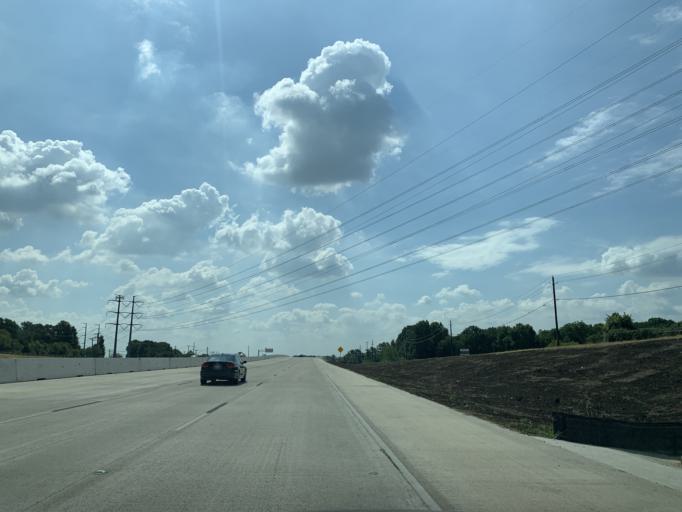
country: US
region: Texas
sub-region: Tarrant County
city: Lakeside
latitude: 32.8580
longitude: -97.5166
